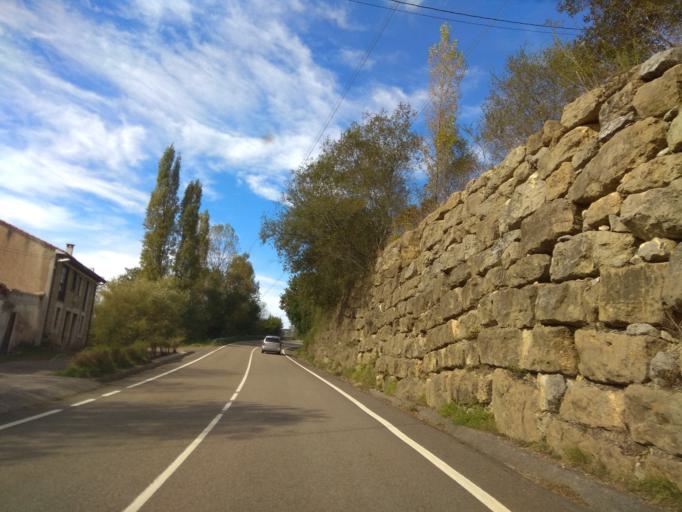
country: ES
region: Cantabria
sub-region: Provincia de Cantabria
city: San Vicente de la Barquera
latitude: 43.3260
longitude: -4.4821
